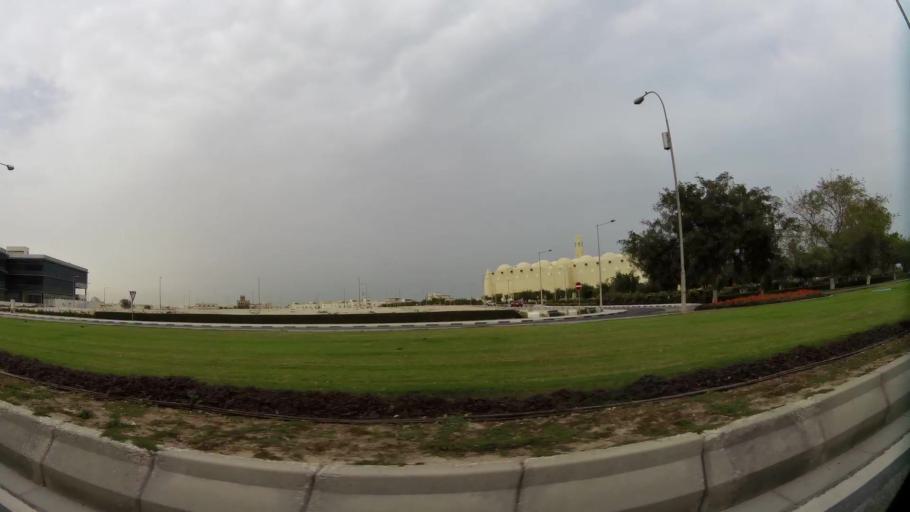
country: QA
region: Baladiyat ad Dawhah
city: Doha
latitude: 25.3149
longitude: 51.5029
